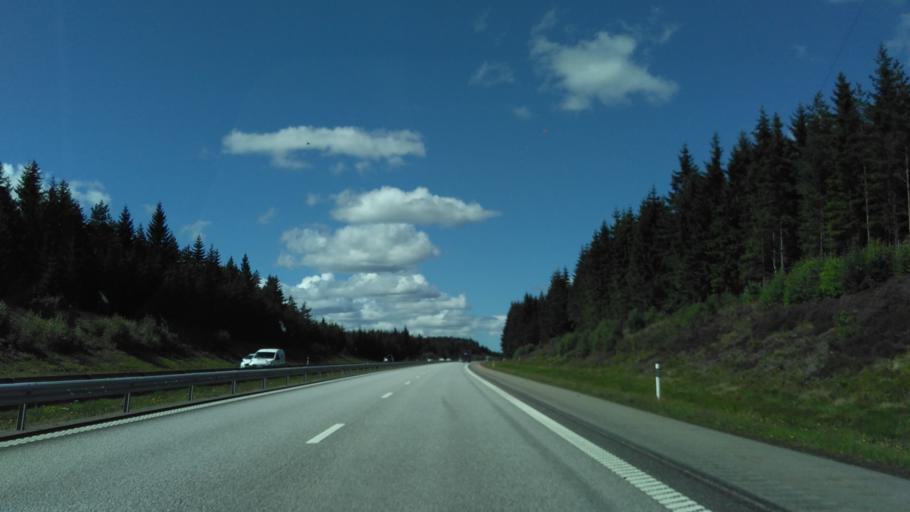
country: SE
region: Vaestra Goetaland
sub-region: Harryda Kommun
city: Hindas
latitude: 57.6675
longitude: 12.3933
